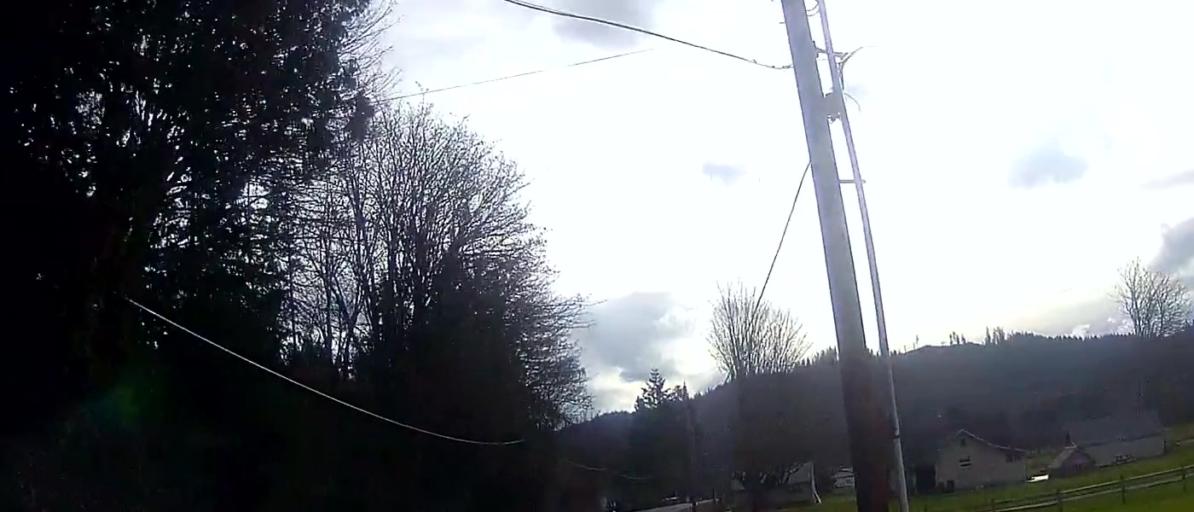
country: US
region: Washington
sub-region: Skagit County
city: Sedro-Woolley
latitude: 48.5688
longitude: -122.2984
